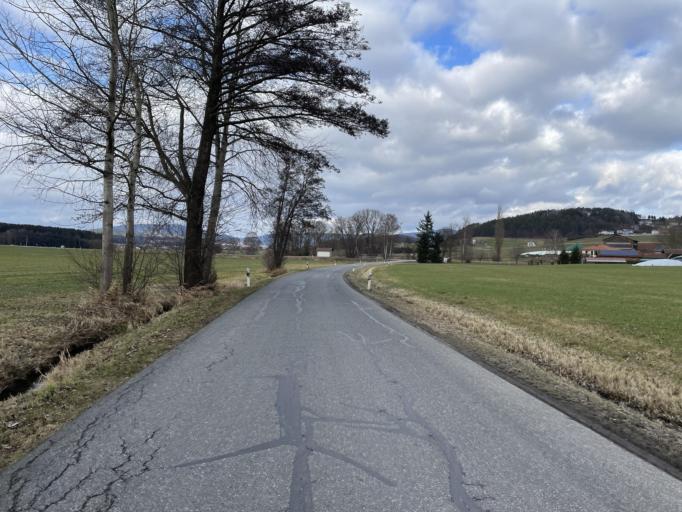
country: DE
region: Bavaria
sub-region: Upper Palatinate
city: Runding
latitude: 49.2310
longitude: 12.7722
